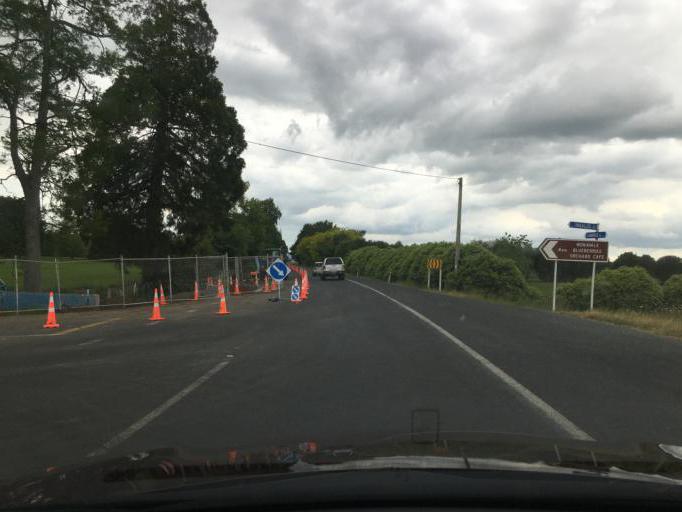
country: NZ
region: Waikato
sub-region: Waipa District
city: Cambridge
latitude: -37.9242
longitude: 175.4346
